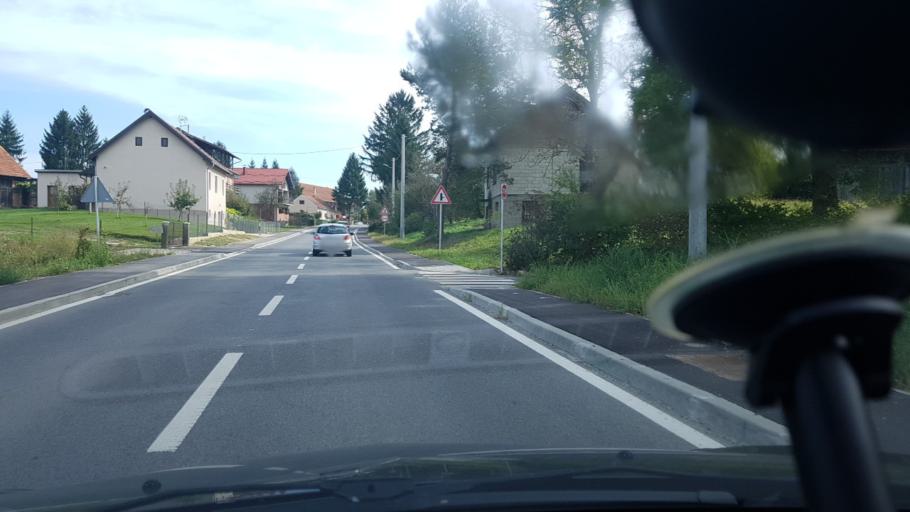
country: HR
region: Krapinsko-Zagorska
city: Marija Bistrica
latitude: 46.0521
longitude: 16.1303
